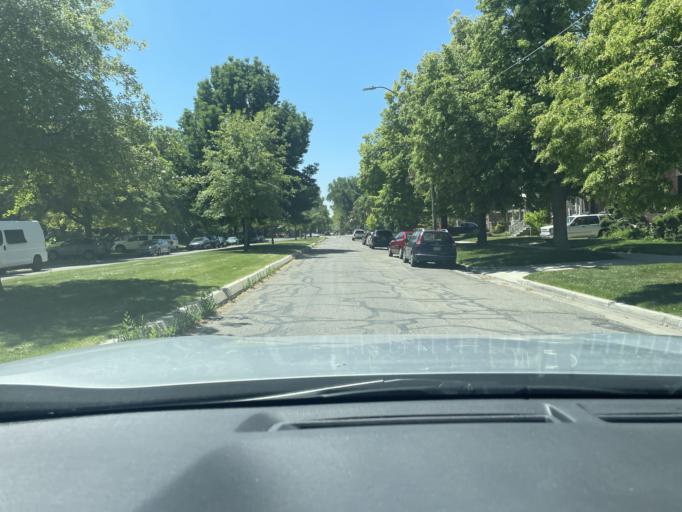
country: US
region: Utah
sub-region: Salt Lake County
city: Salt Lake City
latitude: 40.7512
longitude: -111.8740
